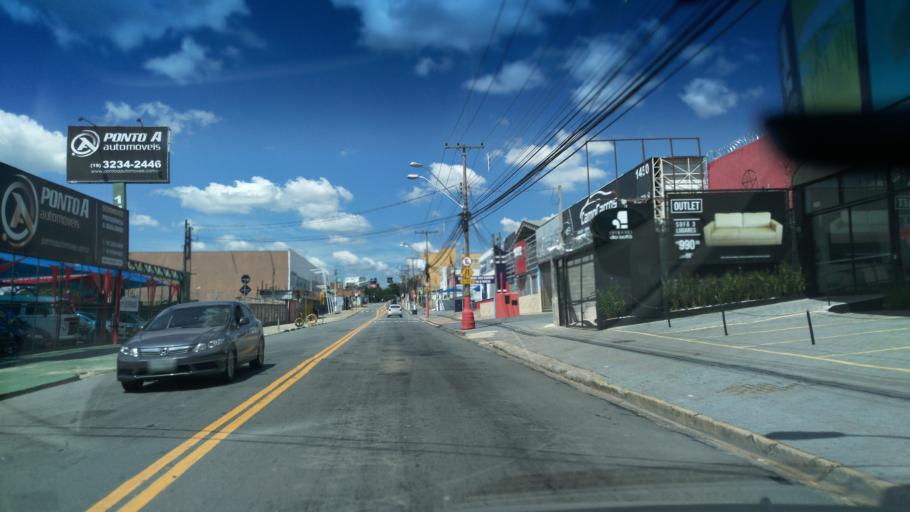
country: BR
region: Sao Paulo
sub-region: Campinas
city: Campinas
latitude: -22.9237
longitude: -47.0466
